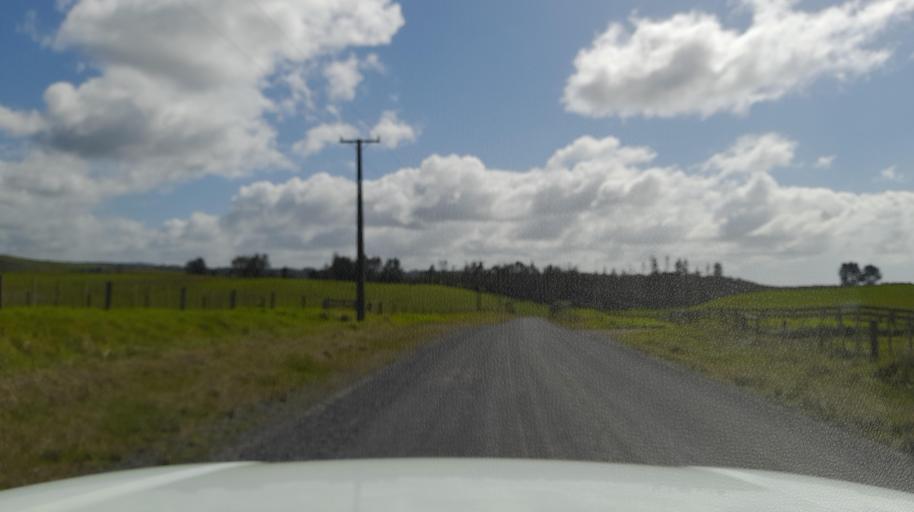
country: NZ
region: Northland
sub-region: Far North District
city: Kerikeri
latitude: -35.2206
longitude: 173.8705
